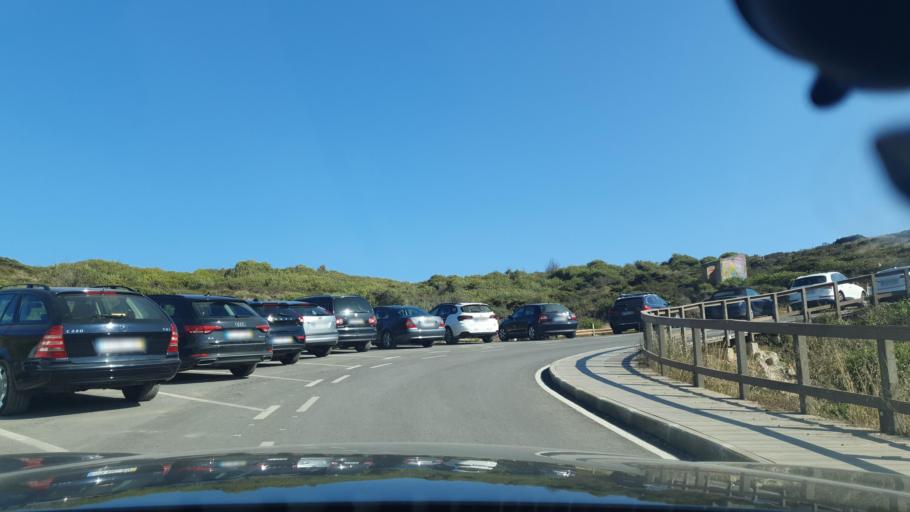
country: PT
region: Beja
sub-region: Odemira
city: Sao Teotonio
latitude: 37.4393
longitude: -8.7990
